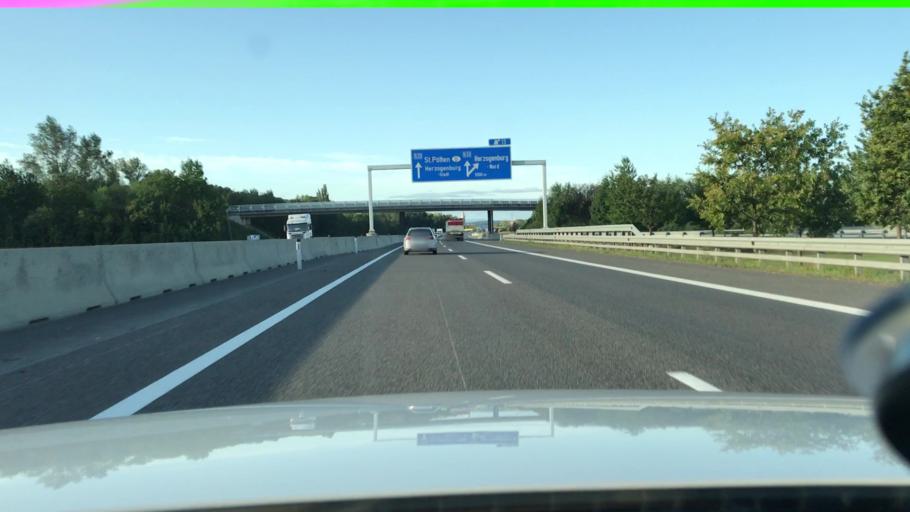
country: AT
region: Lower Austria
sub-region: Politischer Bezirk Sankt Polten
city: Herzogenburg
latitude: 48.3095
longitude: 15.7143
